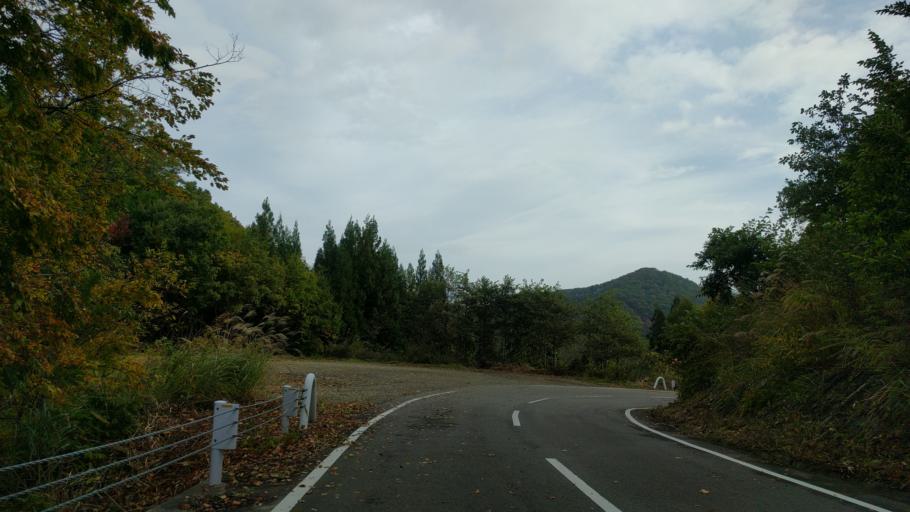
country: JP
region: Fukushima
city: Kitakata
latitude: 37.3845
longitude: 139.6982
